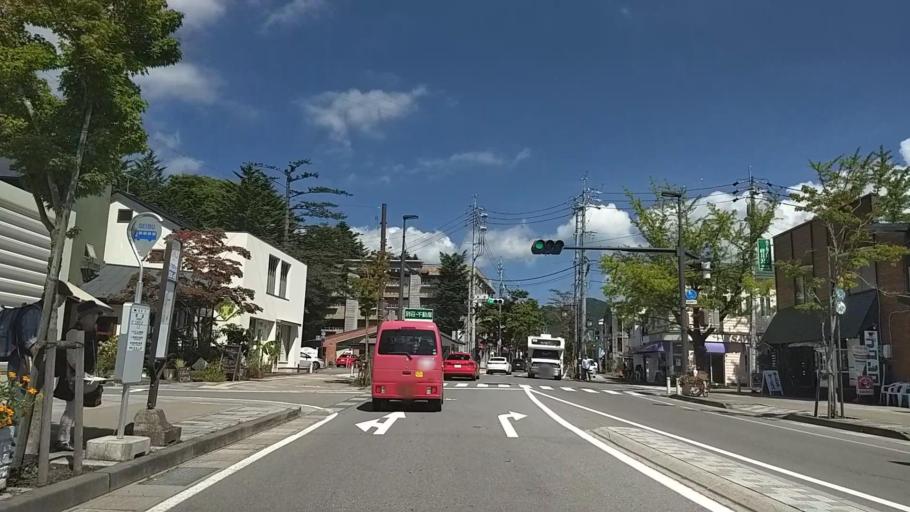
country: JP
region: Nagano
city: Saku
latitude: 36.3482
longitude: 138.6344
